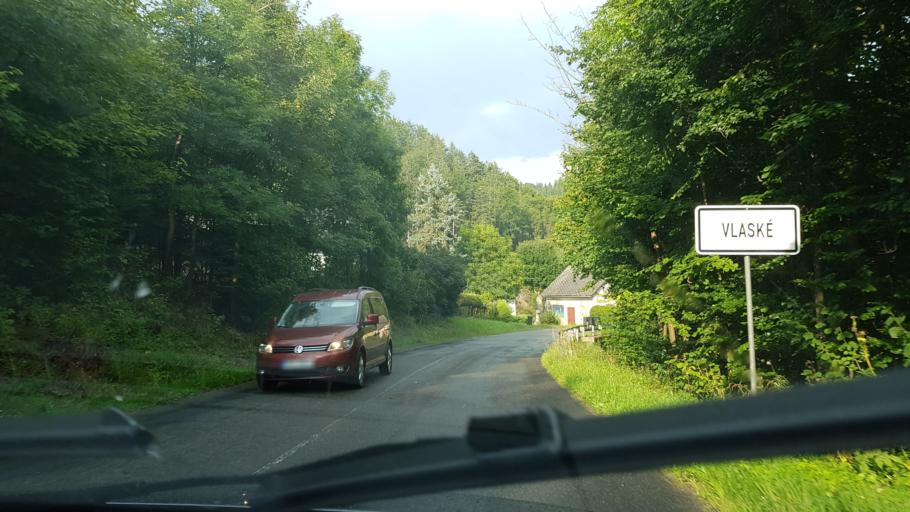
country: CZ
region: Olomoucky
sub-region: Okres Sumperk
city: Hanusovice
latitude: 50.0895
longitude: 16.8906
